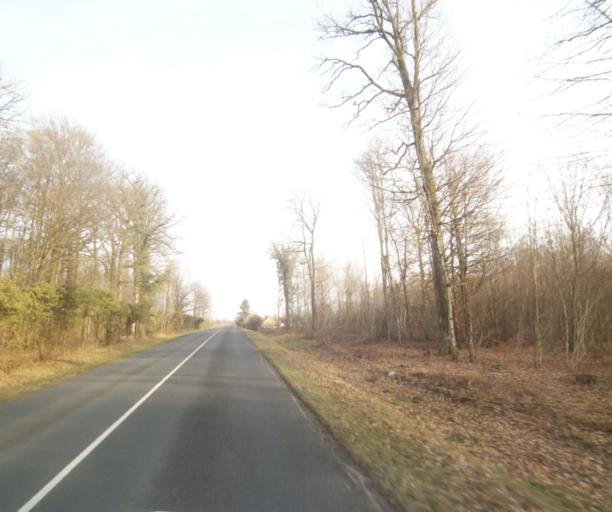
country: FR
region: Champagne-Ardenne
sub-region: Departement de la Haute-Marne
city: Chancenay
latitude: 48.6903
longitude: 4.9451
